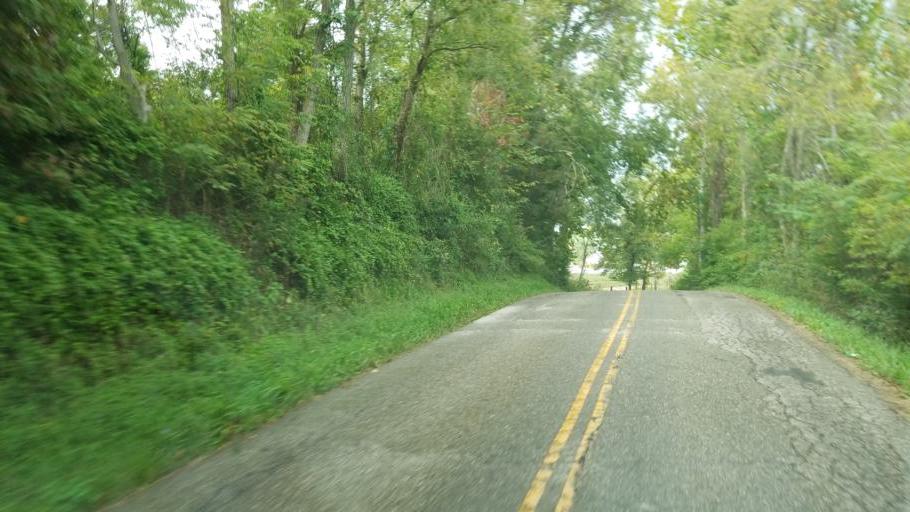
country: US
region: Ohio
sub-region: Jackson County
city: Jackson
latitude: 38.9789
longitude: -82.6459
